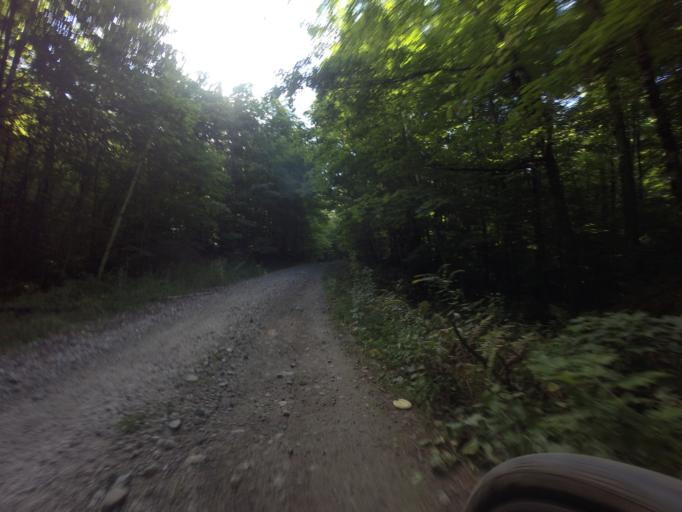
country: CA
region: Ontario
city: Arnprior
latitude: 45.1893
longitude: -76.5150
